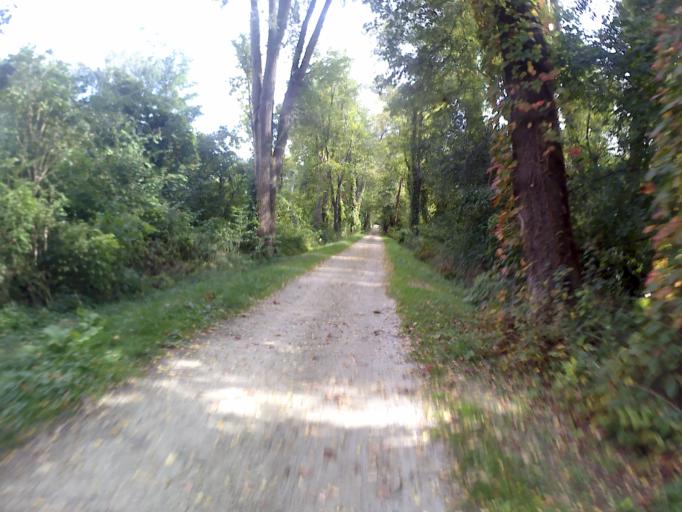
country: US
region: Illinois
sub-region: DuPage County
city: West Chicago
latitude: 41.9117
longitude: -88.1985
